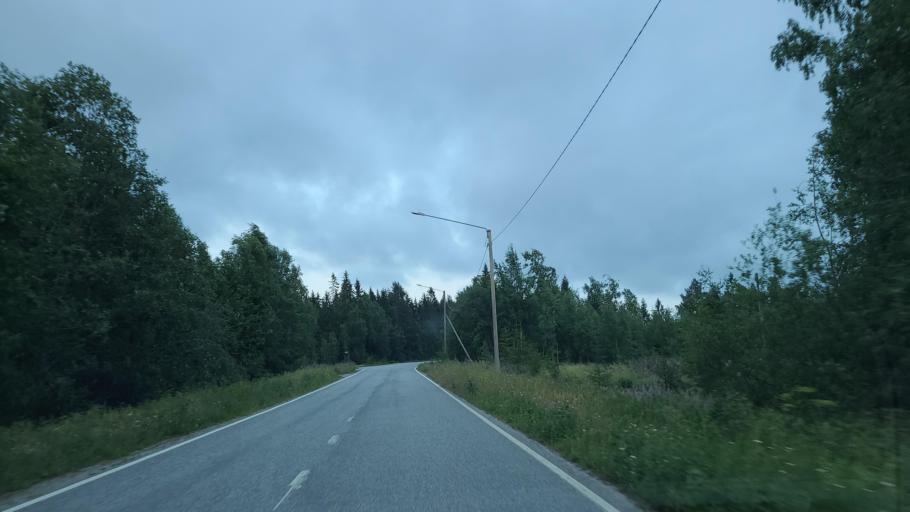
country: FI
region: Ostrobothnia
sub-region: Vaasa
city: Replot
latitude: 63.2804
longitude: 21.1313
